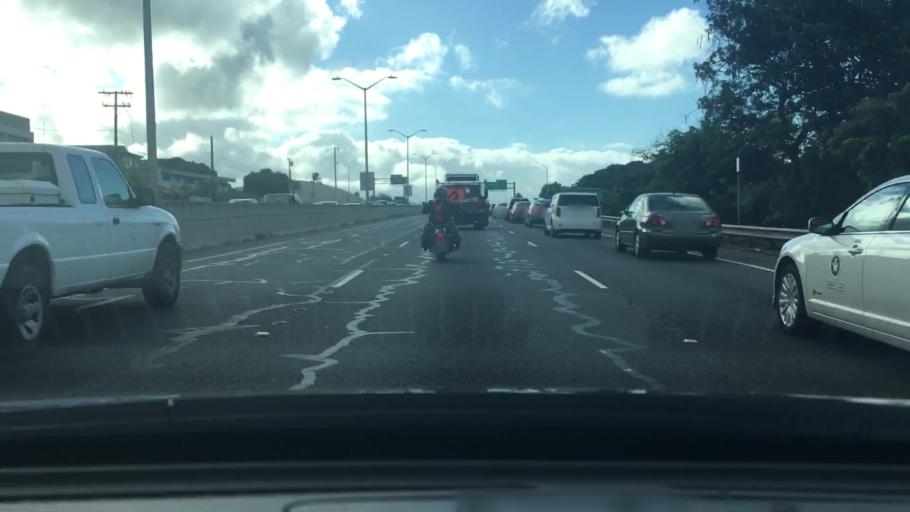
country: US
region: Hawaii
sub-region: Honolulu County
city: Honolulu
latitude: 21.2958
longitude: -157.8235
